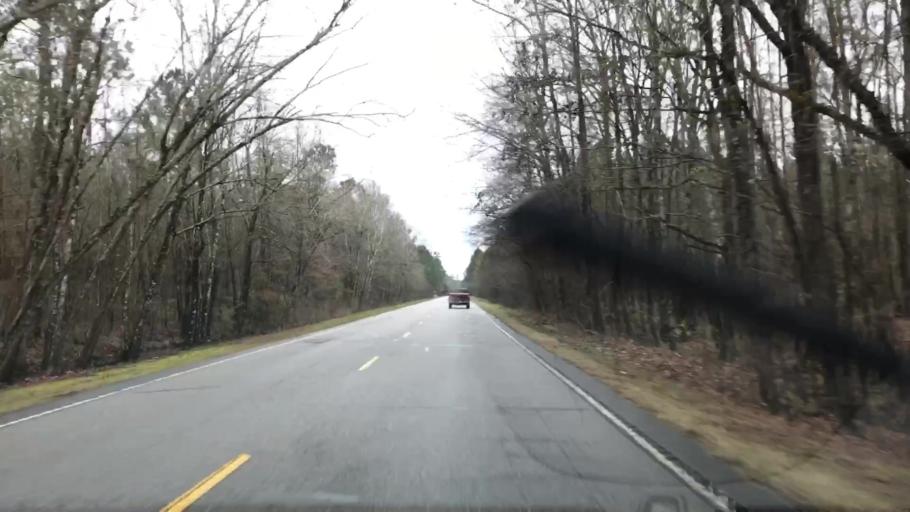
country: US
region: South Carolina
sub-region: Williamsburg County
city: Andrews
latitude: 33.5284
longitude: -79.4885
